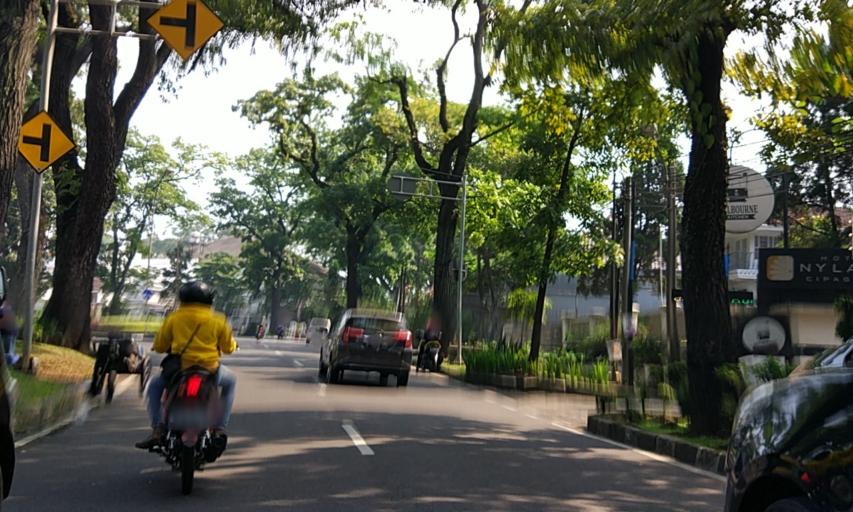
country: ID
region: West Java
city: Bandung
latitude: -6.9030
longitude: 107.6028
